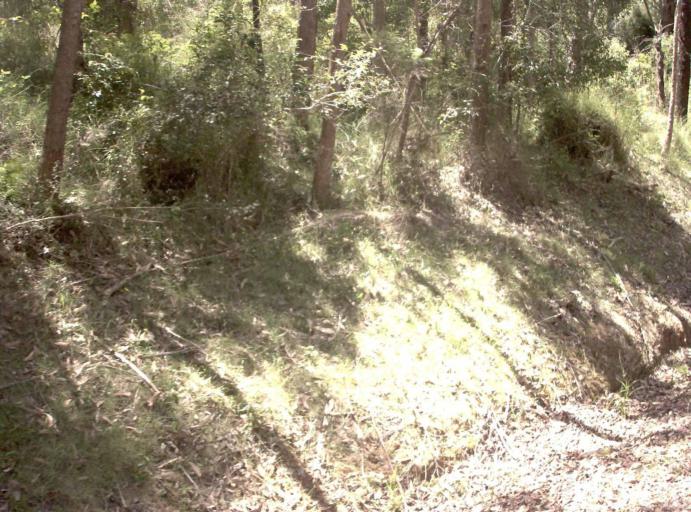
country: AU
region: New South Wales
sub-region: Bombala
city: Bombala
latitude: -37.4639
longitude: 148.9378
